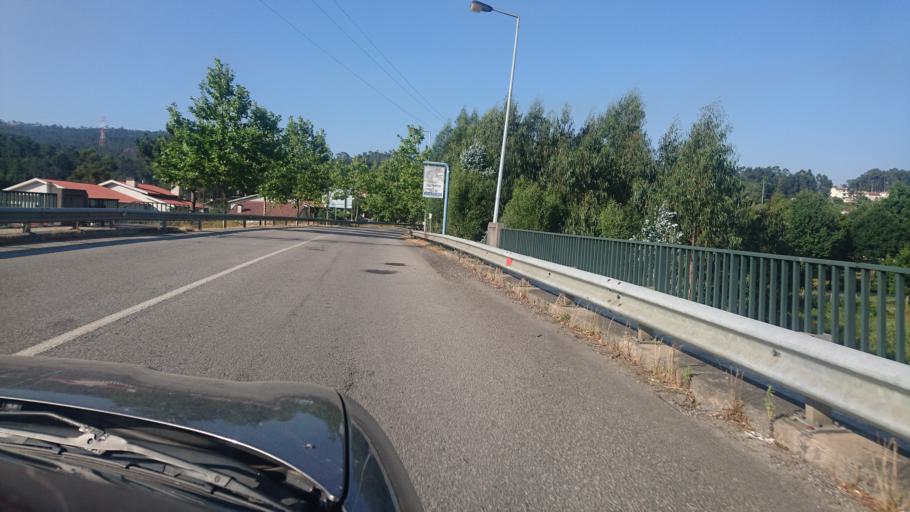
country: PT
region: Porto
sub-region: Paredes
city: Recarei
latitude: 41.1550
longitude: -8.4016
